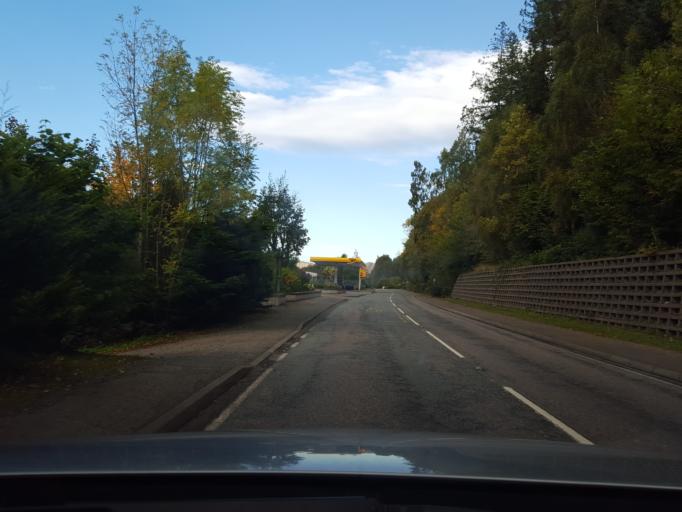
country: GB
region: Scotland
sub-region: Highland
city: Fort William
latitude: 57.2415
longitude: -5.4565
